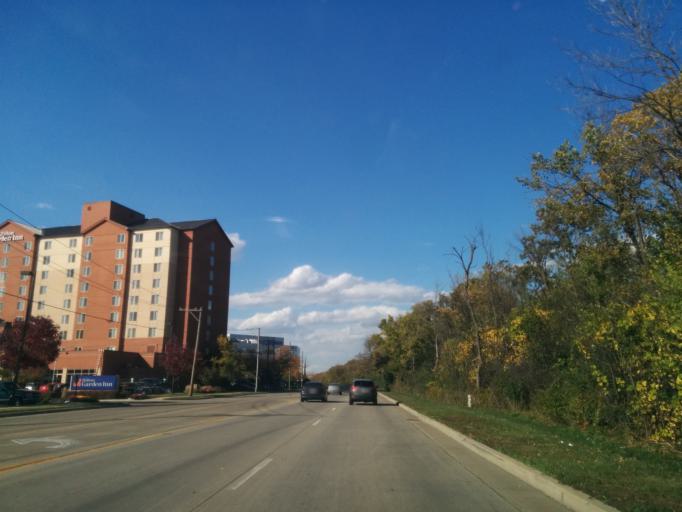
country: US
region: Illinois
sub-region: Cook County
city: Rosemont
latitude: 42.0002
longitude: -87.8634
